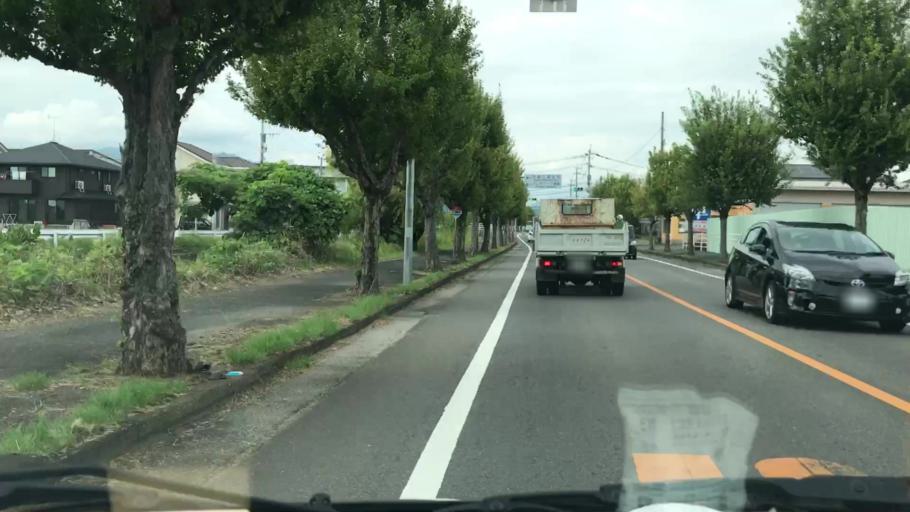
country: JP
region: Saga Prefecture
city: Saga-shi
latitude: 33.2639
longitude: 130.2627
